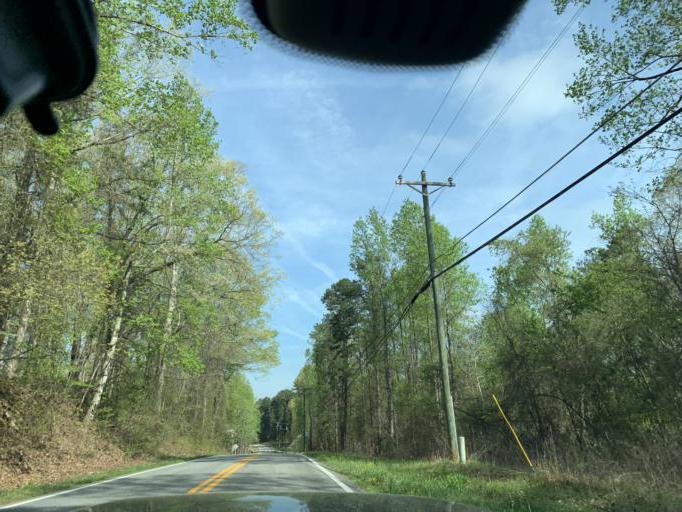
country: US
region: Georgia
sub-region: Forsyth County
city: Cumming
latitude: 34.2089
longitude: -84.0727
